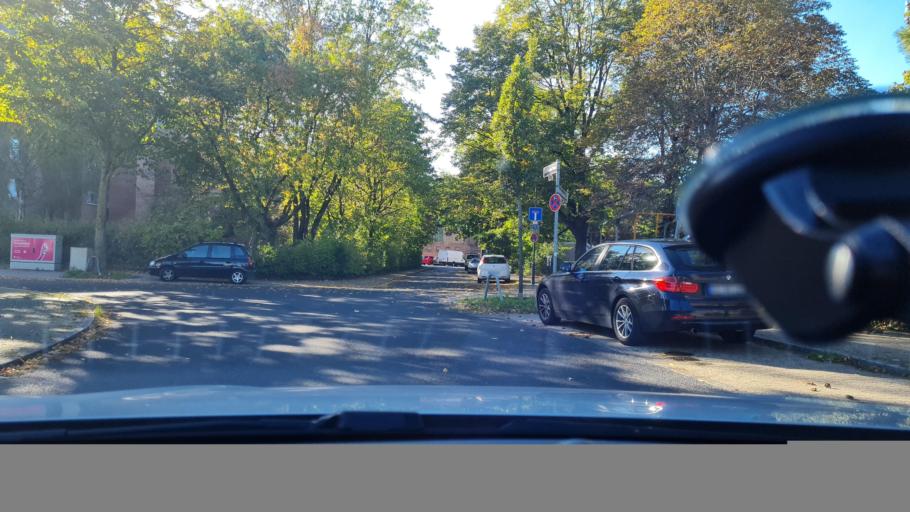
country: DE
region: North Rhine-Westphalia
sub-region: Regierungsbezirk Dusseldorf
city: Hilden
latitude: 51.1335
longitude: 6.9046
